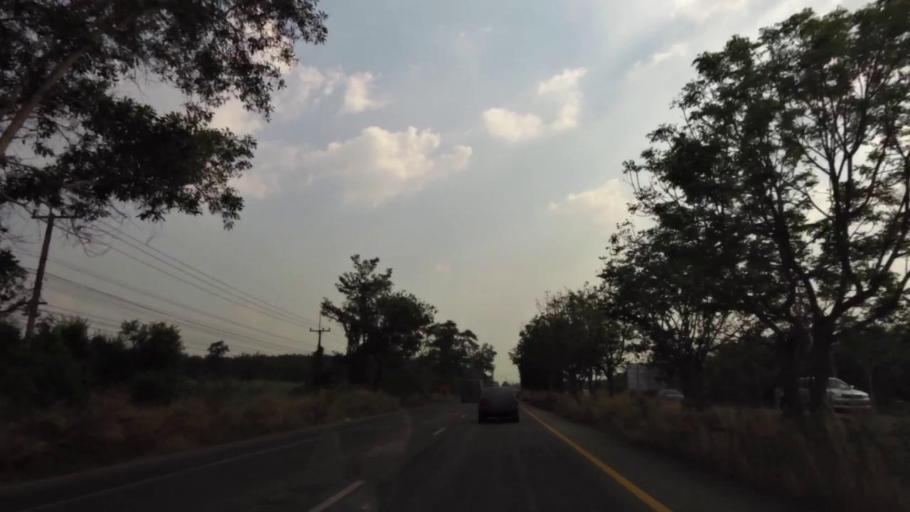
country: TH
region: Rayong
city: Wang Chan
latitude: 12.9960
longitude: 101.4852
